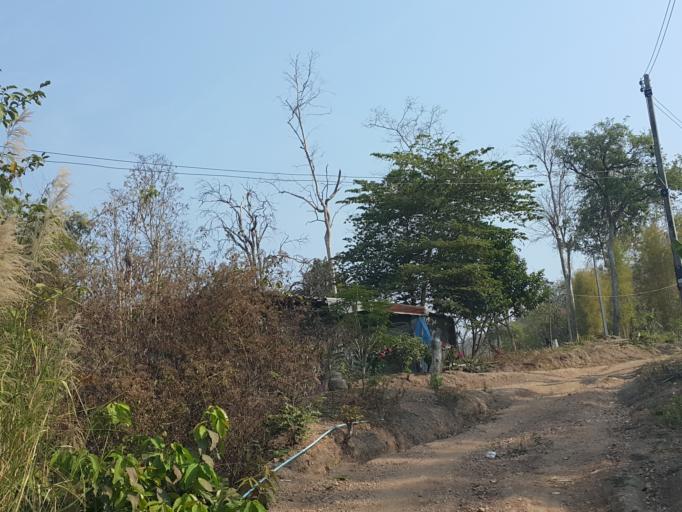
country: TH
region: Chiang Mai
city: Hang Dong
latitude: 18.7398
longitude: 98.8638
